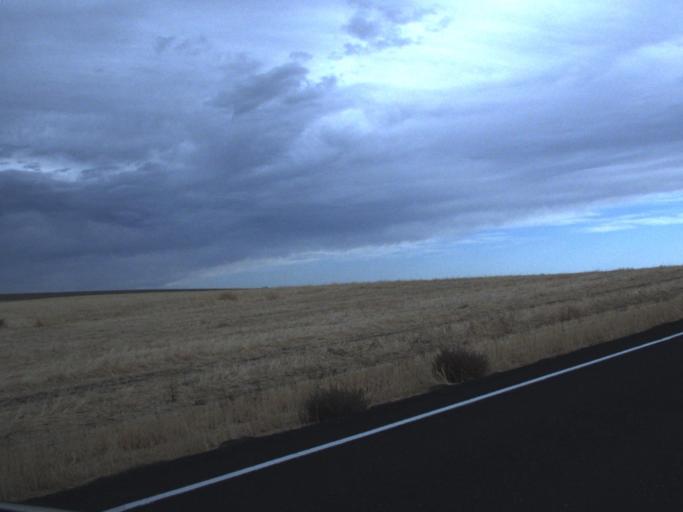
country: US
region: Washington
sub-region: Okanogan County
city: Coulee Dam
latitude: 47.6125
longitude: -118.7369
